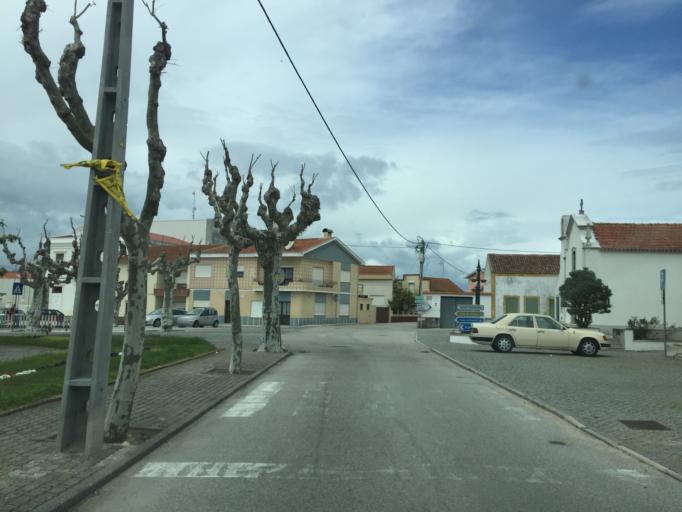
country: PT
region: Coimbra
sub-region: Figueira da Foz
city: Tavarede
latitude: 40.2151
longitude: -8.8497
